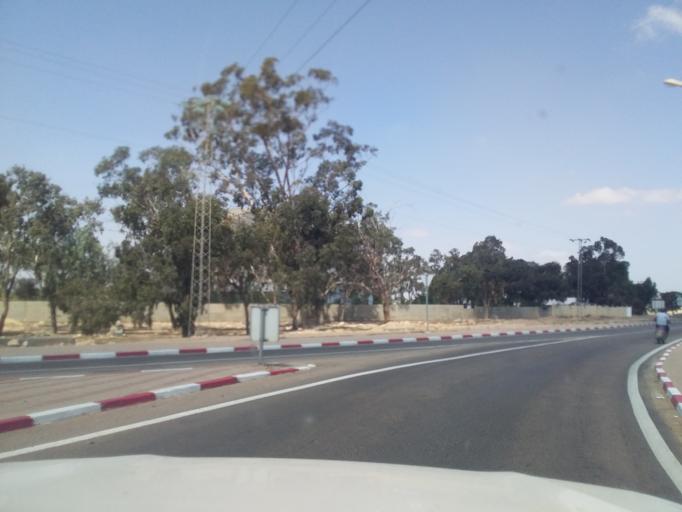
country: TN
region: Madanin
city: Medenine
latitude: 33.5993
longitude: 10.3093
